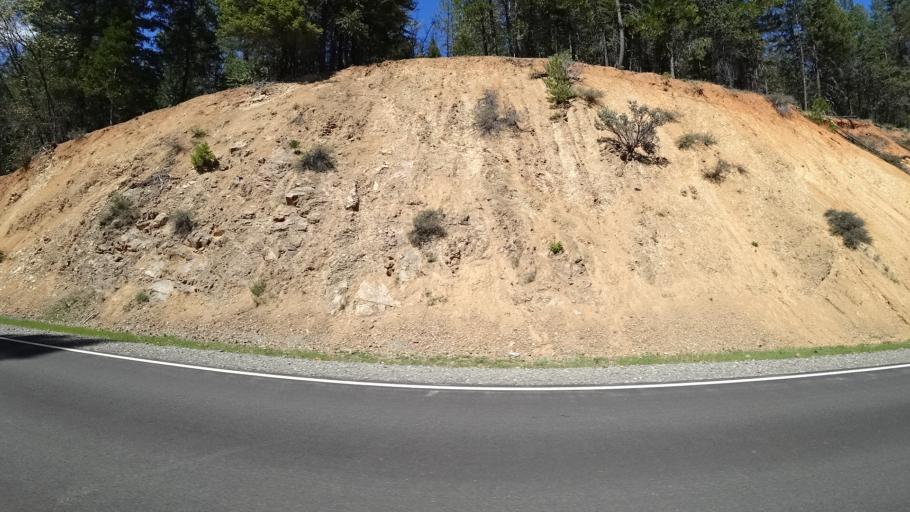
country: US
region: California
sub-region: Trinity County
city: Lewiston
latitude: 40.9058
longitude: -122.7842
